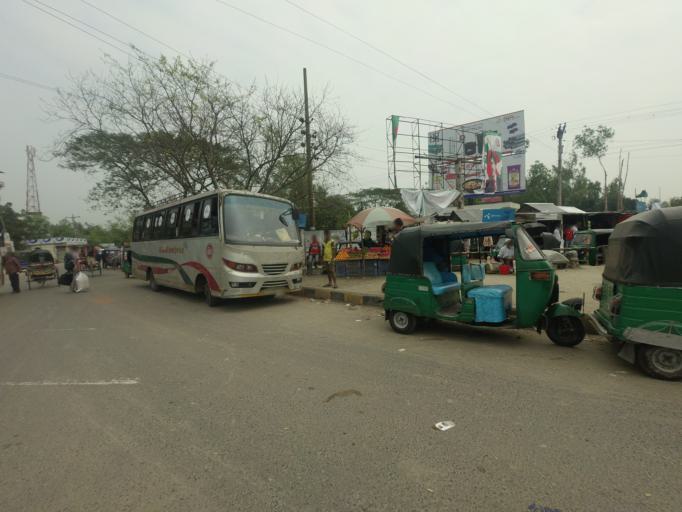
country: BD
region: Rajshahi
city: Sirajganj
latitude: 24.3953
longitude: 89.6917
